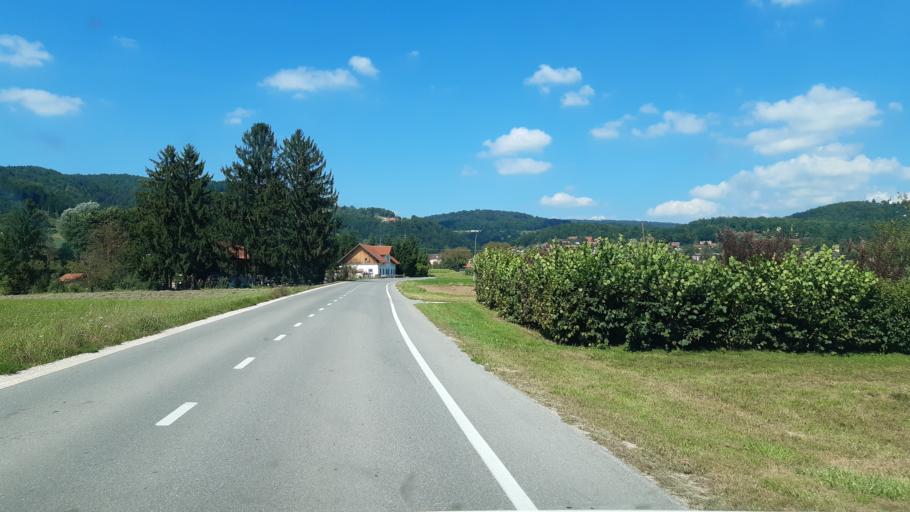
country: SI
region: Ivancna Gorica
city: Ivancna Gorica
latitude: 45.9490
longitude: 14.8030
